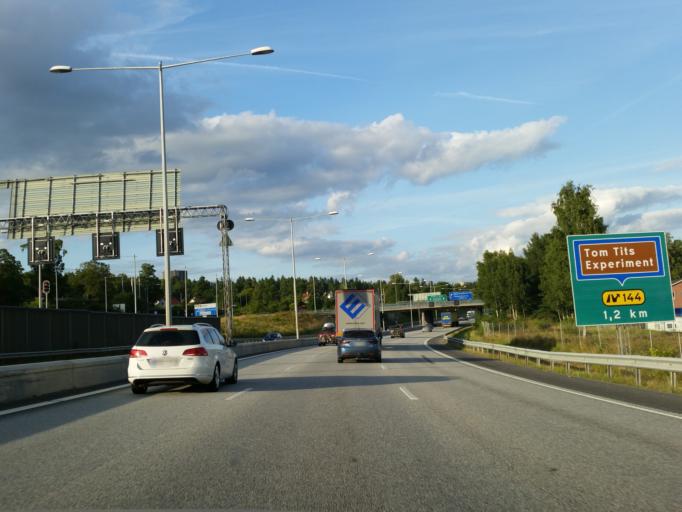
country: SE
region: Stockholm
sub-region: Sodertalje Kommun
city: Soedertaelje
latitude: 59.1879
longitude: 17.6455
